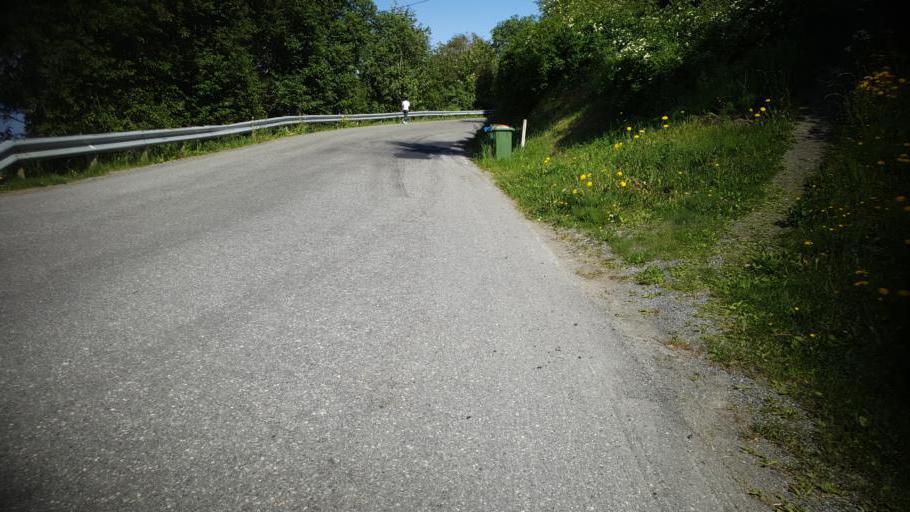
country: NO
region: Sor-Trondelag
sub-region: Malvik
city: Malvik
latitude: 63.4320
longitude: 10.5973
